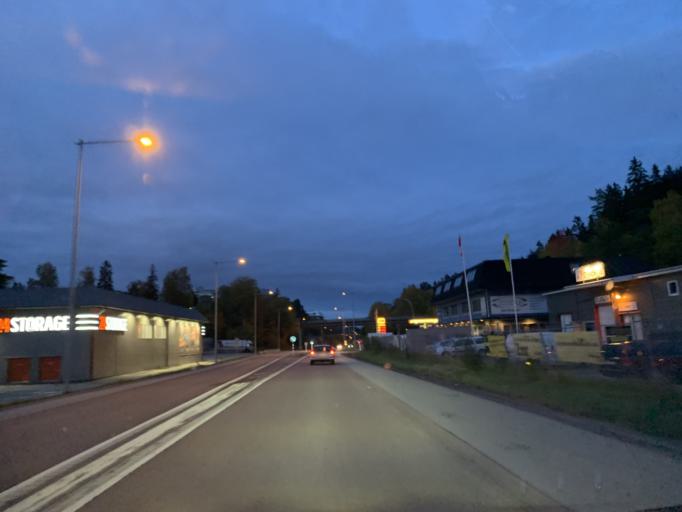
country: SE
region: Stockholm
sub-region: Botkyrka Kommun
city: Tumba
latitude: 59.1949
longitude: 17.8291
